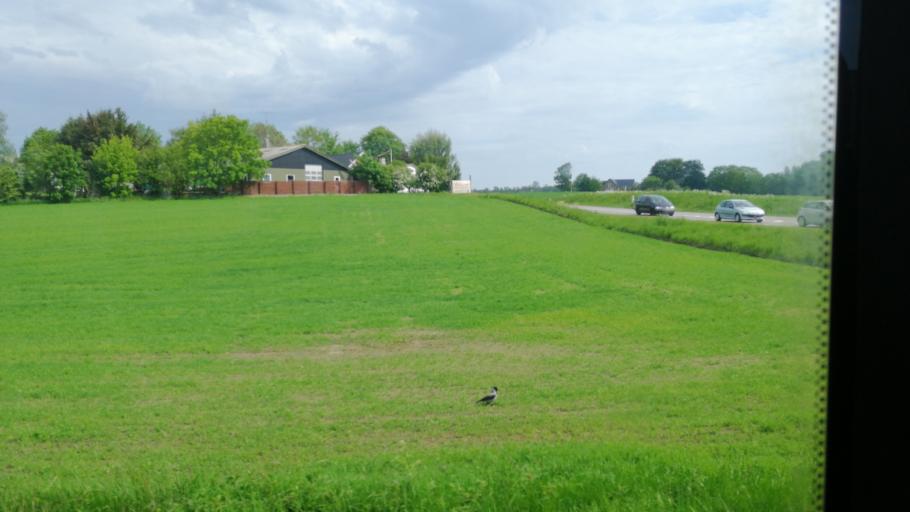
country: DK
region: Capital Region
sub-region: Gribskov Kommune
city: Gilleleje
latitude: 56.1008
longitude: 12.3334
